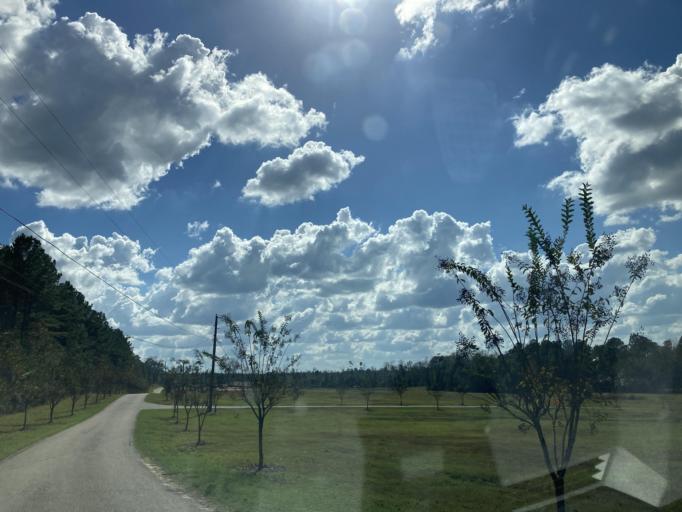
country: US
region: Mississippi
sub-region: Lamar County
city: West Hattiesburg
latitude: 31.2662
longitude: -89.3670
